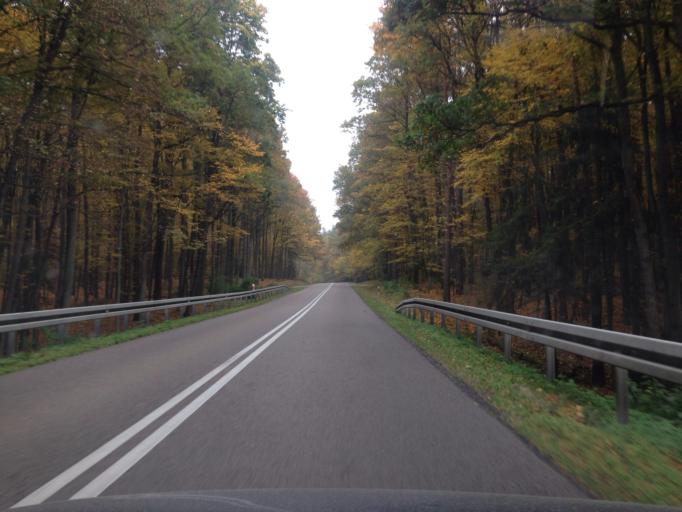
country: PL
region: Kujawsko-Pomorskie
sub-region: Powiat brodnicki
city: Gorzno
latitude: 53.2450
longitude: 19.7002
